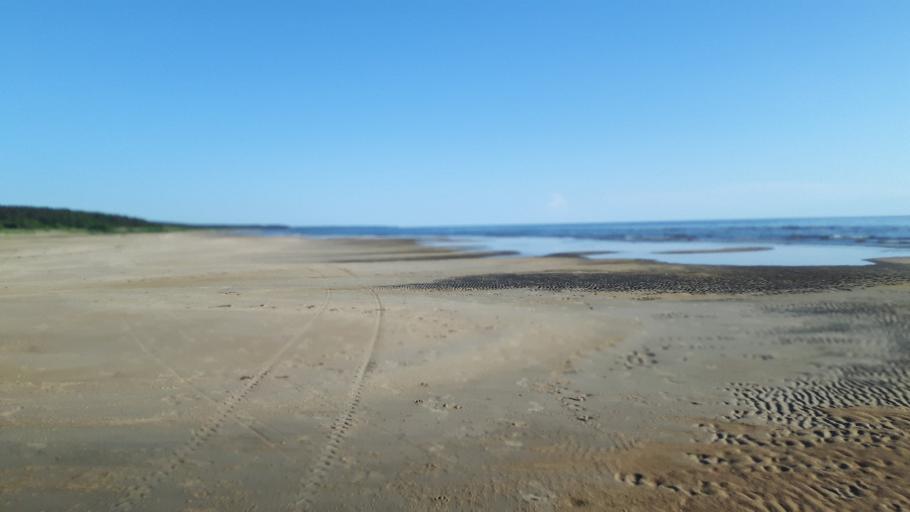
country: LV
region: Salacgrivas
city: Salacgriva
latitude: 57.6895
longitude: 24.3550
